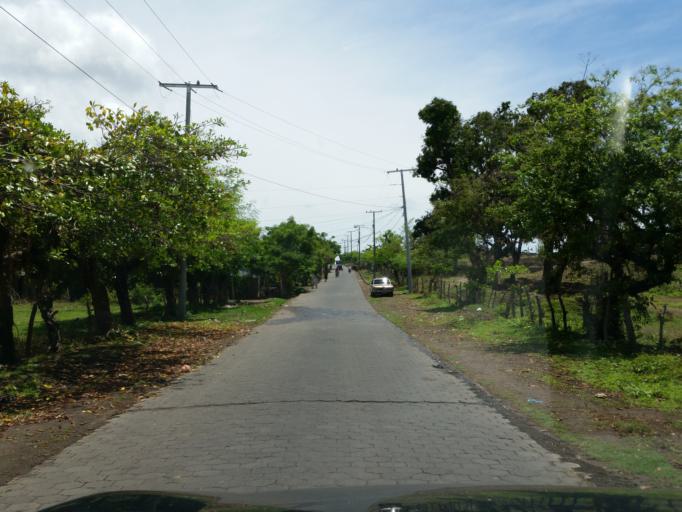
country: NI
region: Granada
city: Granada
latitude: 11.9225
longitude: -85.9464
